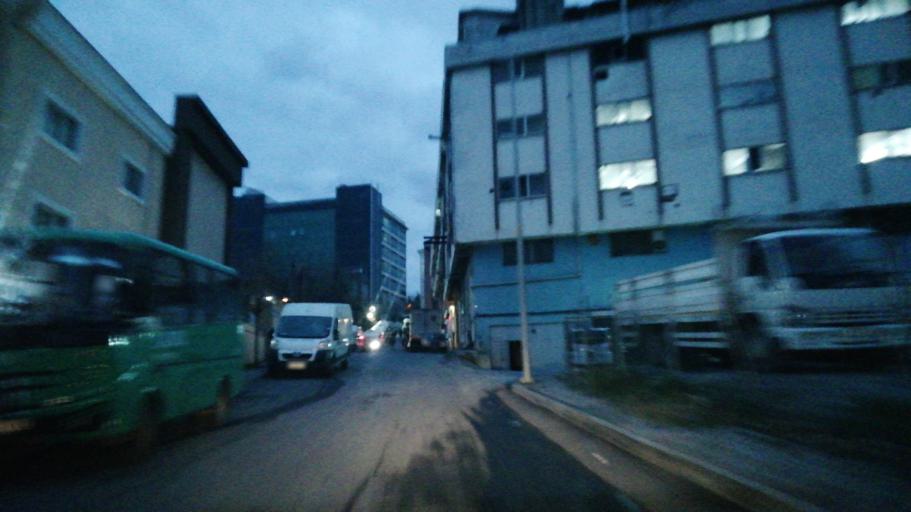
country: TR
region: Istanbul
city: Mahmutbey
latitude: 41.0212
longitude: 28.8248
